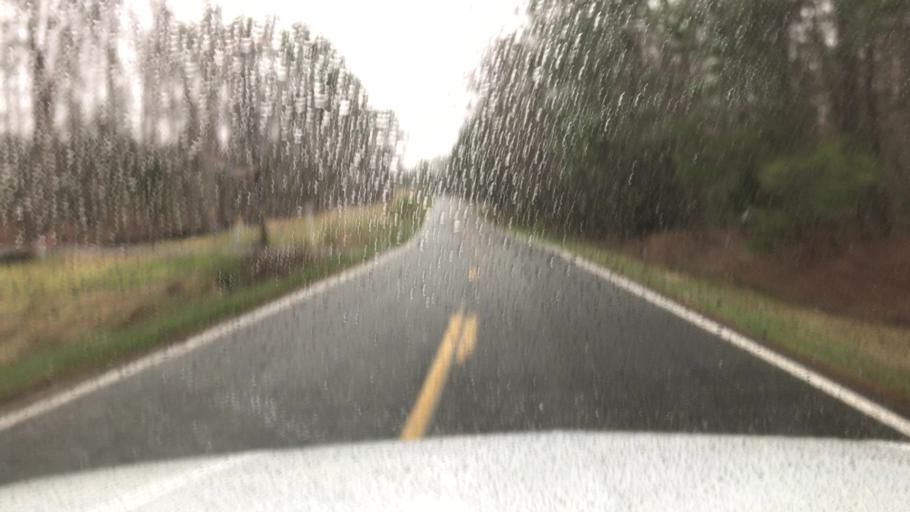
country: US
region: Virginia
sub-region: Henrico County
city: Short Pump
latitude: 37.6469
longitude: -77.6786
